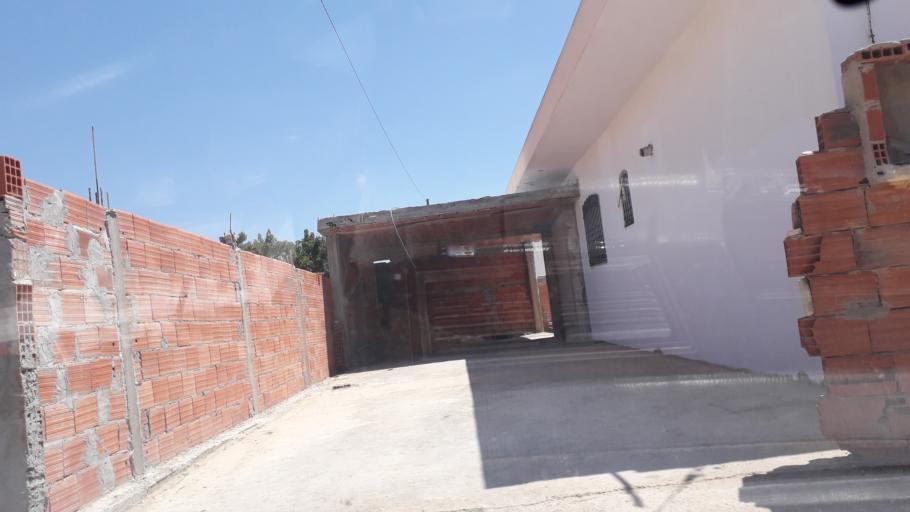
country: TN
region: Safaqis
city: Al Qarmadah
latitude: 34.8270
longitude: 10.7696
